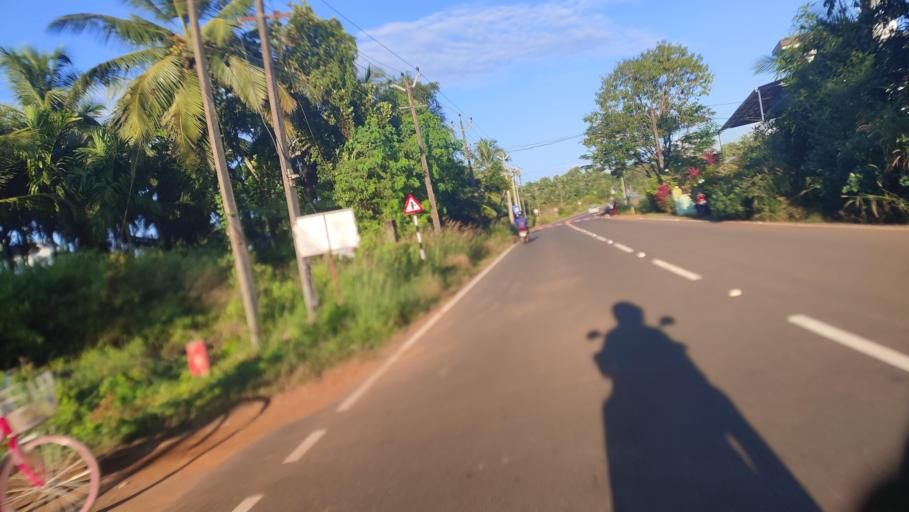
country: IN
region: Kerala
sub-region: Kasaragod District
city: Kasaragod
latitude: 12.4666
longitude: 75.0789
